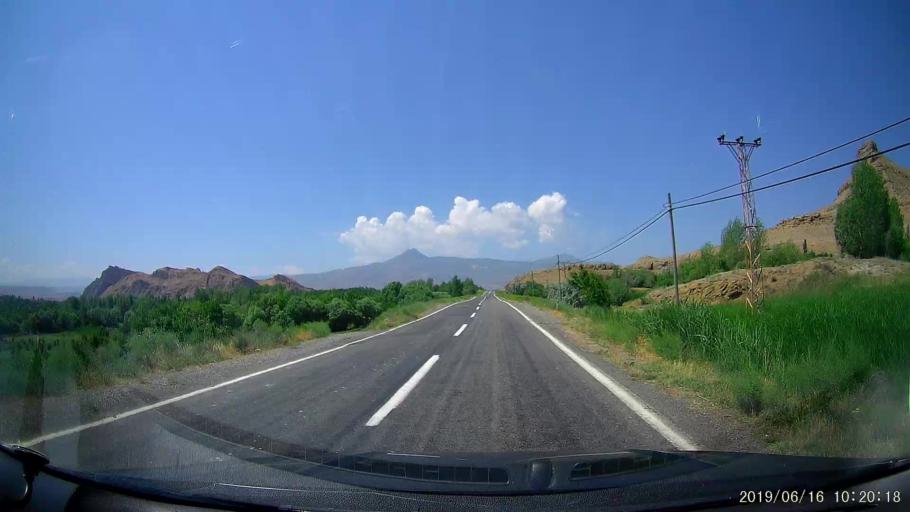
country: TR
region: Igdir
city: Tuzluca
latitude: 40.1490
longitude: 43.6491
